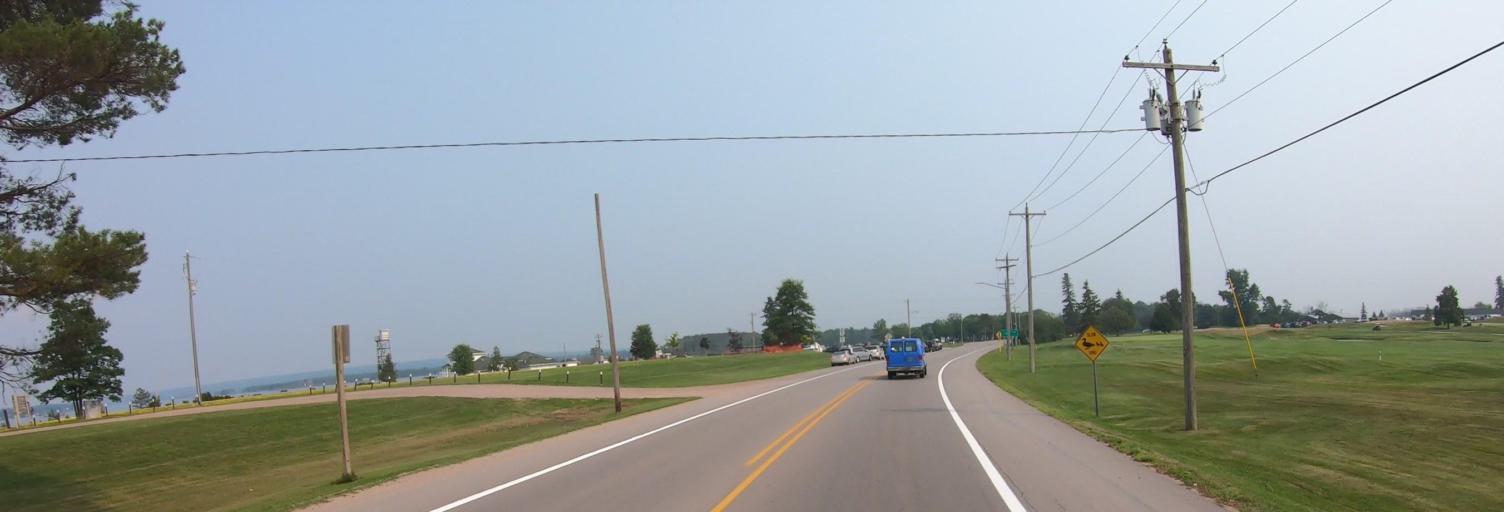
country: US
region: Michigan
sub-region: Chippewa County
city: Sault Ste. Marie
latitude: 46.4866
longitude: -84.3053
